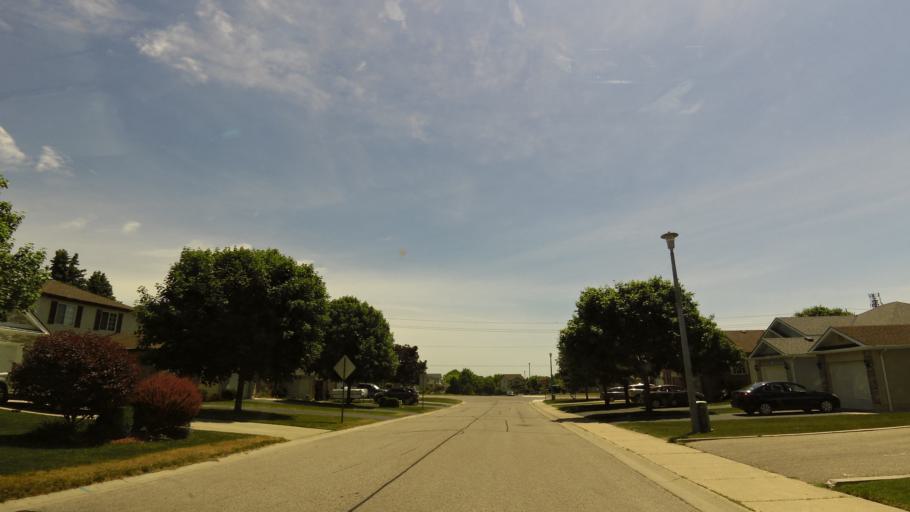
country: CA
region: Ontario
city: Ingersoll
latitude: 42.8828
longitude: -80.7221
